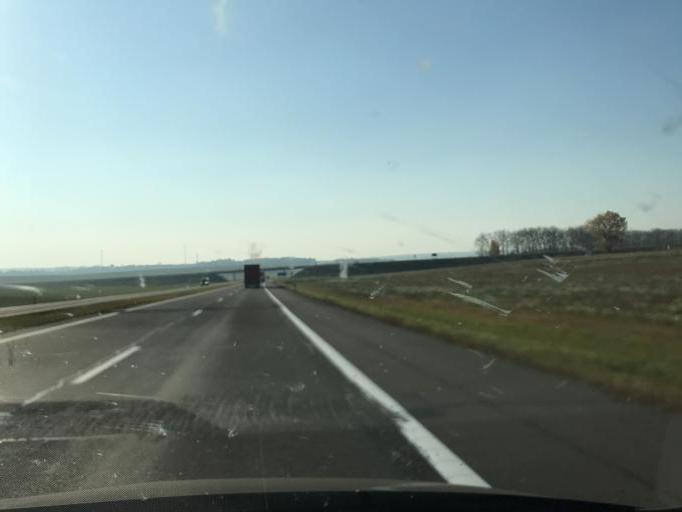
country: BY
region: Minsk
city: Snow
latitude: 53.2690
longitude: 26.2950
